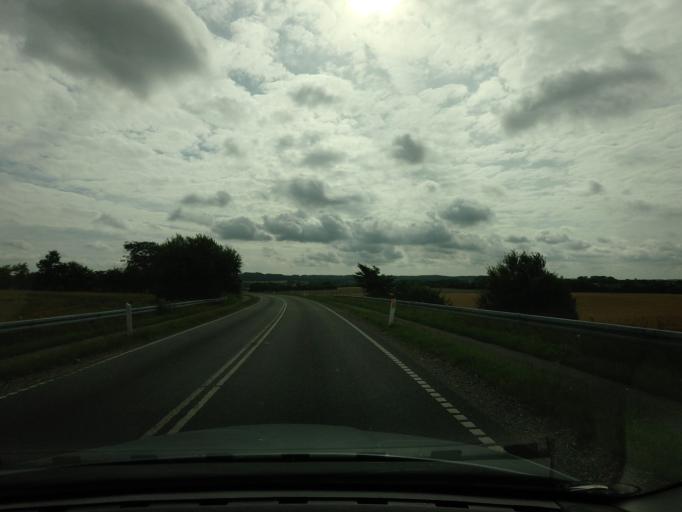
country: DK
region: North Denmark
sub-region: Bronderslev Kommune
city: Hjallerup
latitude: 57.2701
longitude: 10.1530
